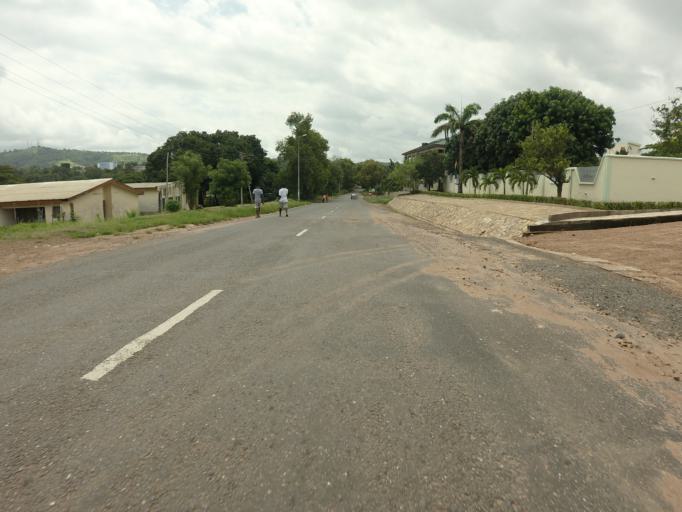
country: GH
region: Volta
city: Ho
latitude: 6.5966
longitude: 0.4631
